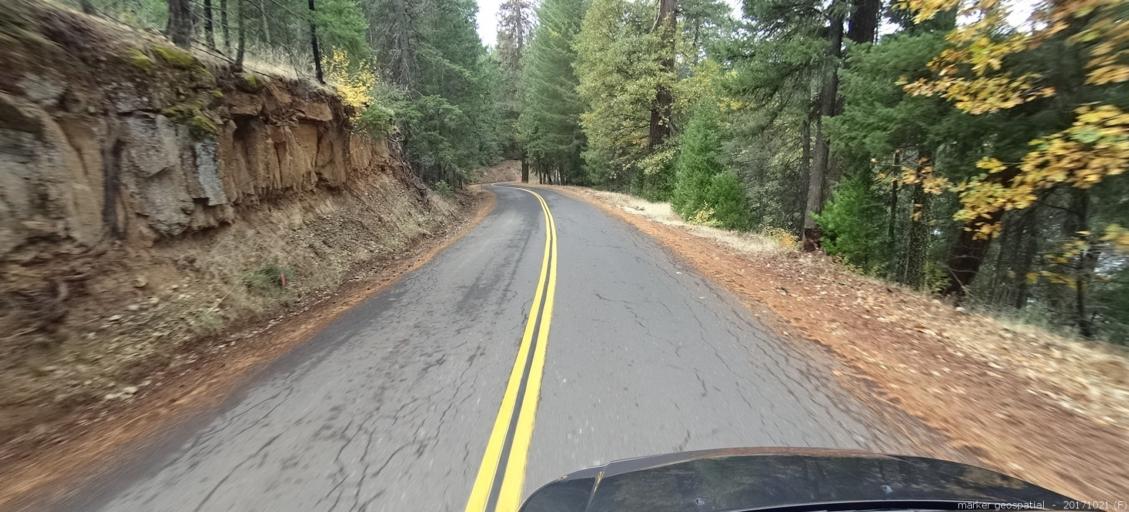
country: US
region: California
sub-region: Shasta County
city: Burney
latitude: 41.0196
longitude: -121.6676
